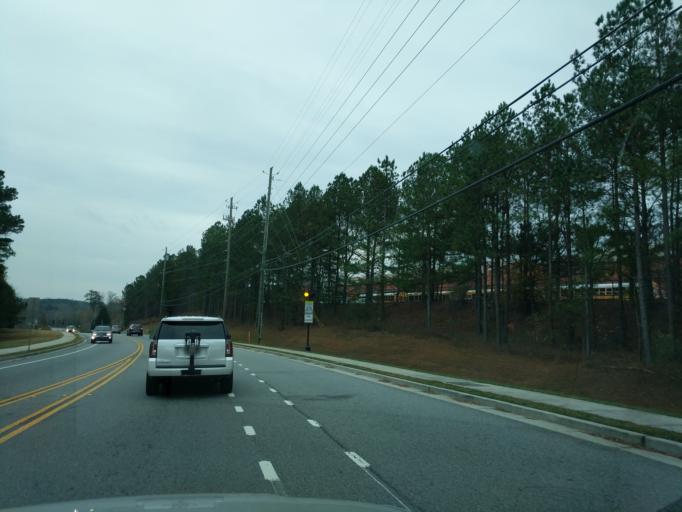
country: US
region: Georgia
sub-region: Fulton County
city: Alpharetta
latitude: 34.0533
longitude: -84.2748
